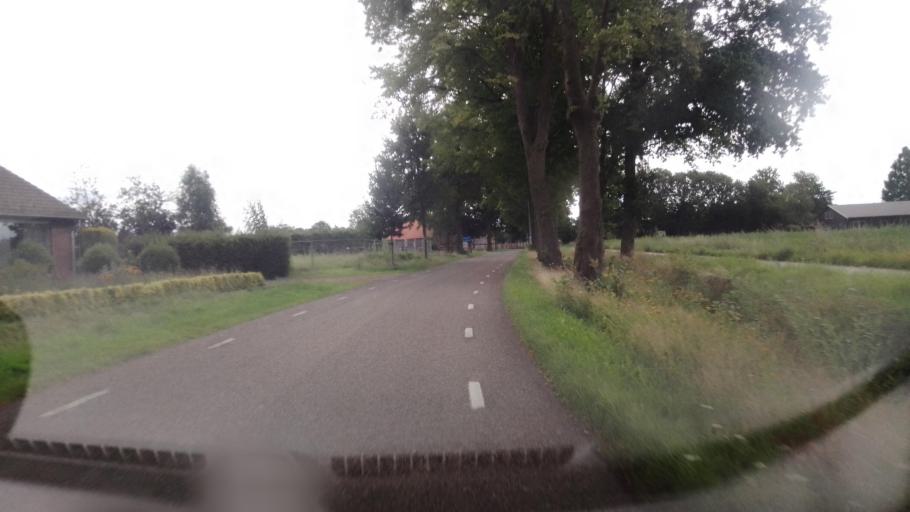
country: NL
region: Limburg
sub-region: Gemeente Peel en Maas
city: Maasbree
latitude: 51.4167
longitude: 5.9945
